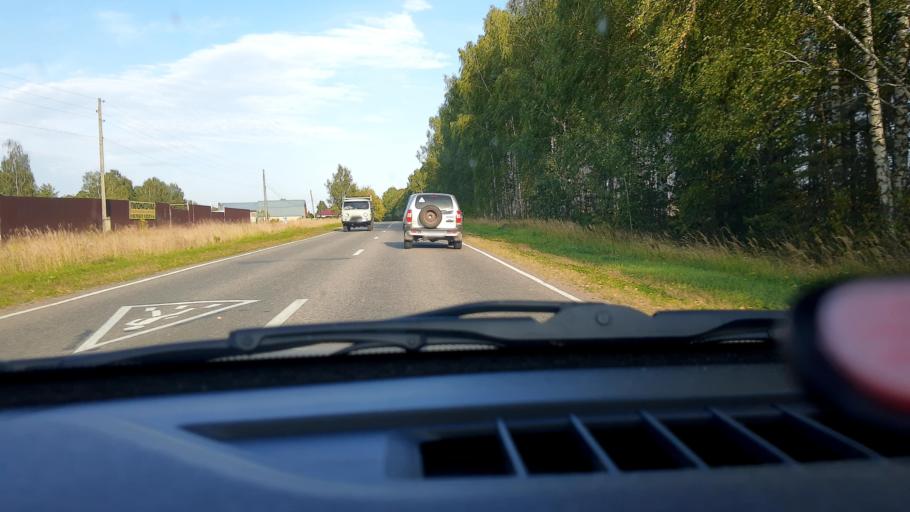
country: RU
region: Nizjnij Novgorod
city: Gorodets
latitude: 56.6677
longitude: 43.6129
